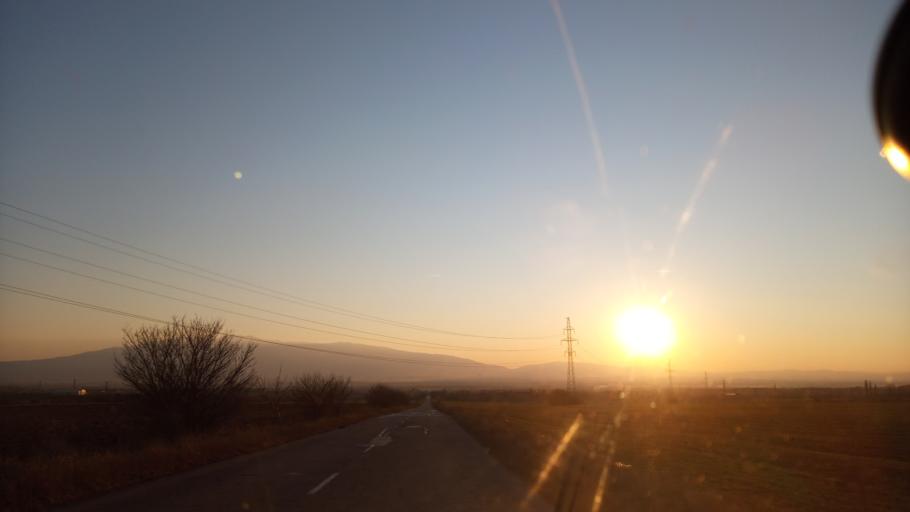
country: BG
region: Sofia-Capital
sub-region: Stolichna Obshtina
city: Bukhovo
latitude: 42.7757
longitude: 23.5071
